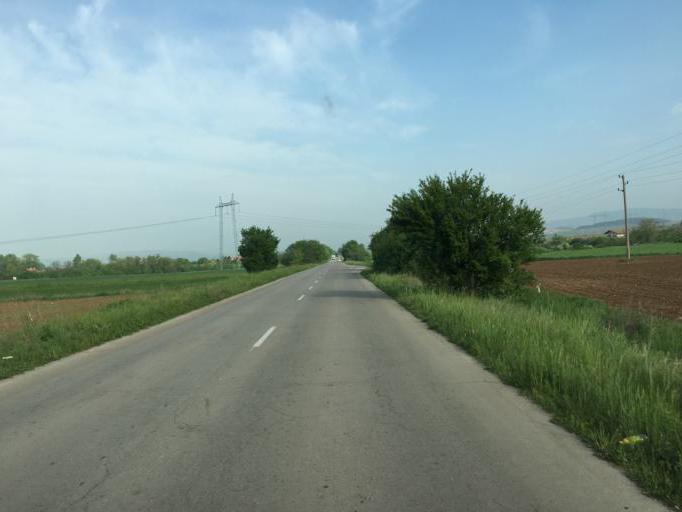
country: BG
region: Pernik
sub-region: Obshtina Radomir
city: Radomir
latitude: 42.4845
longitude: 23.0534
